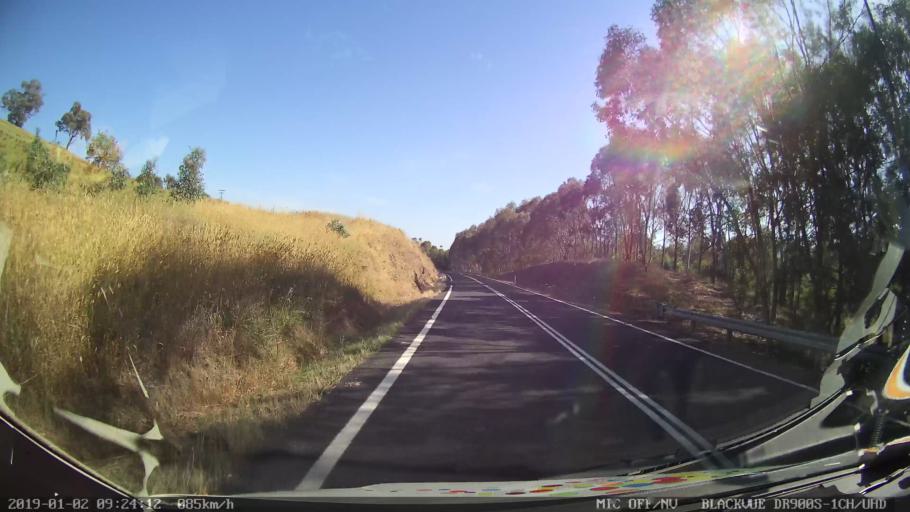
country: AU
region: New South Wales
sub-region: Tumut Shire
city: Tumut
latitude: -35.3801
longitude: 148.2919
